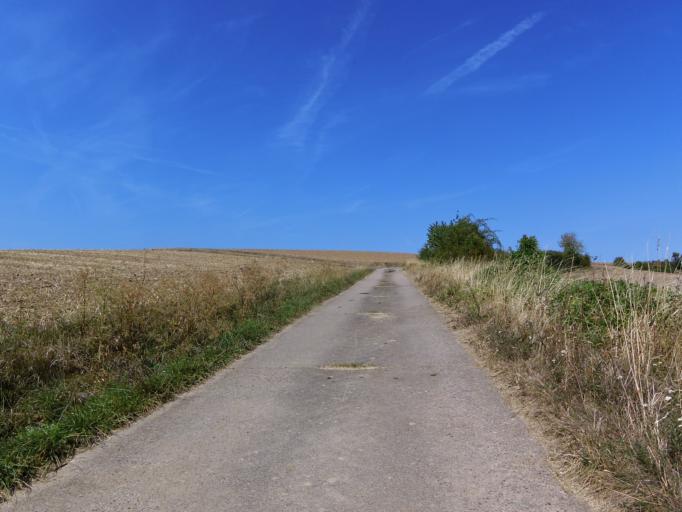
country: DE
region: Bavaria
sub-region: Regierungsbezirk Unterfranken
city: Theilheim
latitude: 49.7646
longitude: 10.0298
